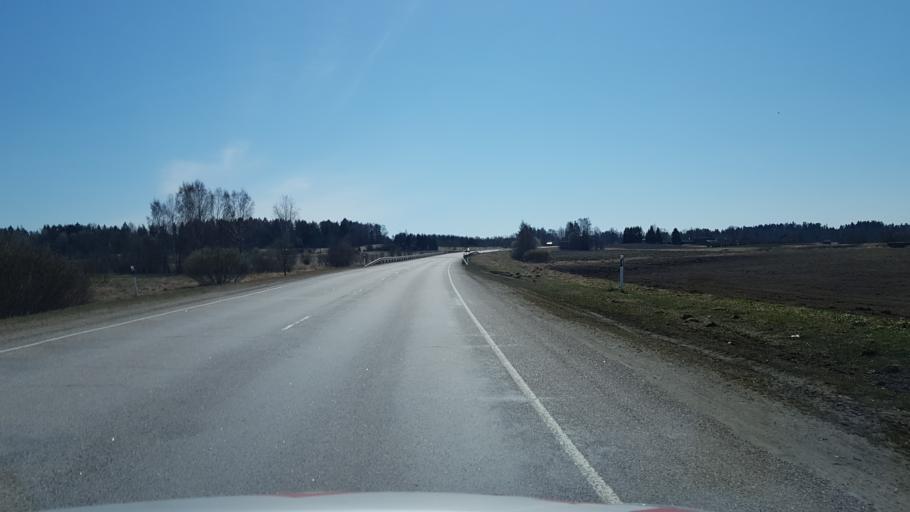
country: EE
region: Ida-Virumaa
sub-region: Johvi vald
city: Johvi
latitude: 59.1508
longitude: 27.3592
